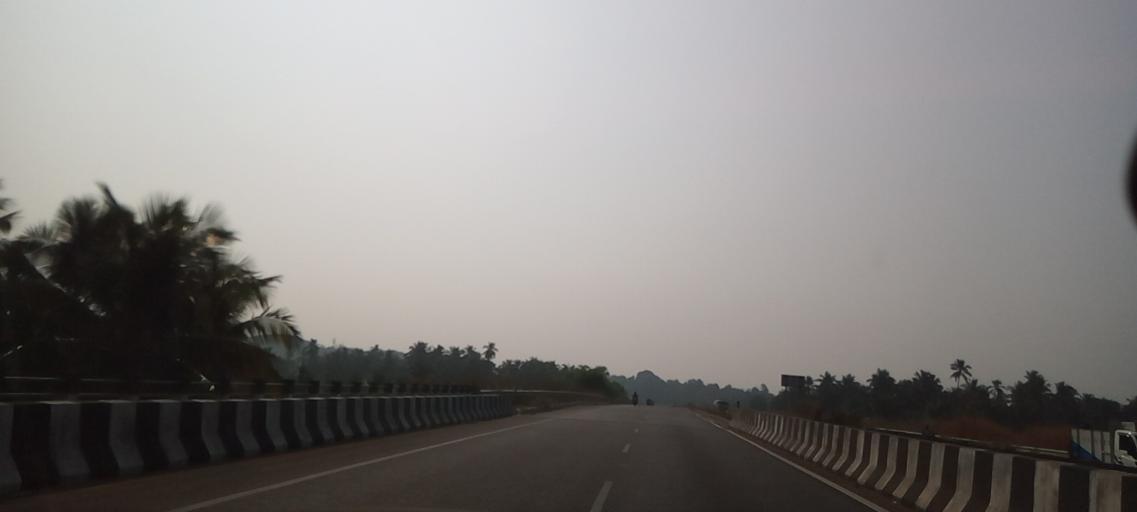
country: IN
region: Karnataka
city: Gangolli
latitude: 13.6822
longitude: 74.6846
